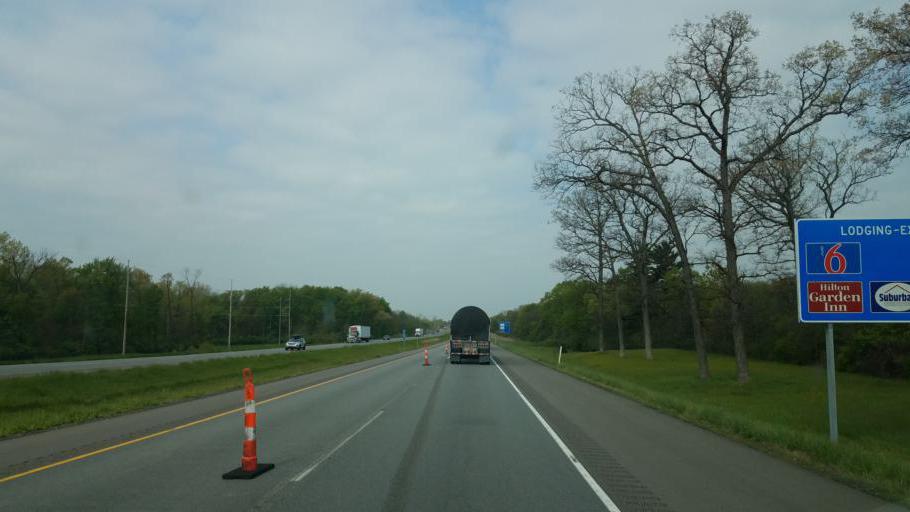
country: US
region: Indiana
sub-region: Saint Joseph County
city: Georgetown
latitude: 41.7164
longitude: -86.2251
